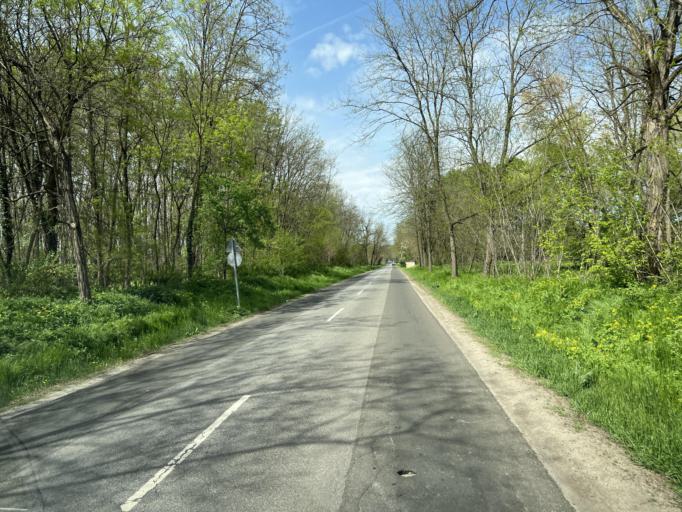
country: HU
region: Pest
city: Albertirsa
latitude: 47.2131
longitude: 19.6097
